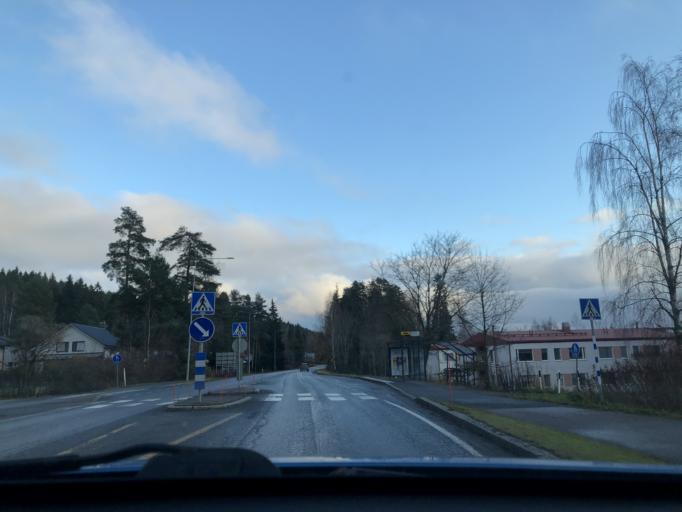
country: FI
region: Pirkanmaa
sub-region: Tampere
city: Kangasala
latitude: 61.4688
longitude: 24.0429
